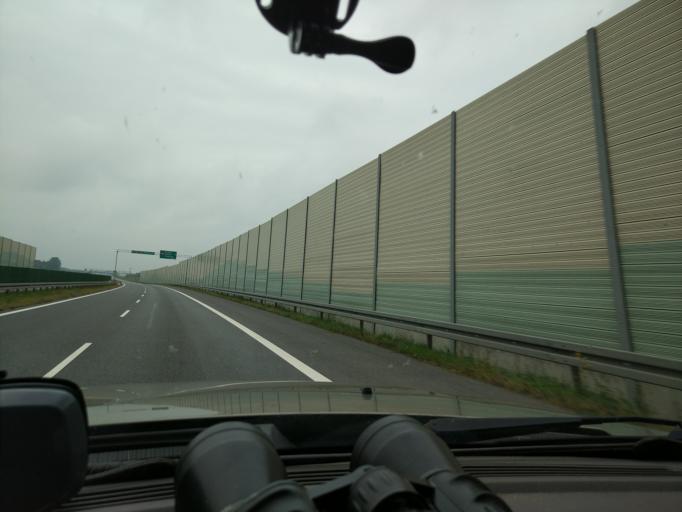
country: PL
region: Podlasie
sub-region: Powiat zambrowski
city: Zambrow
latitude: 52.9674
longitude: 22.2050
